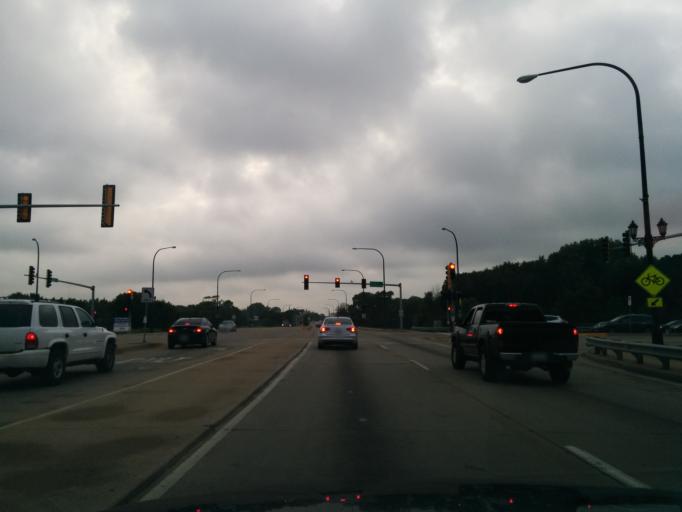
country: US
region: Illinois
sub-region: DuPage County
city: Addison
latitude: 41.9290
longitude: -87.9776
